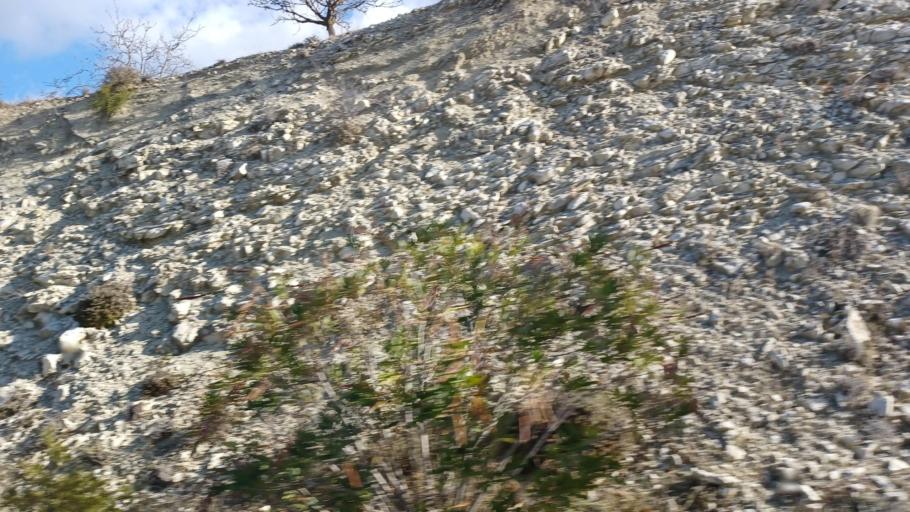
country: CY
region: Limassol
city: Pachna
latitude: 34.8316
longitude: 32.6846
